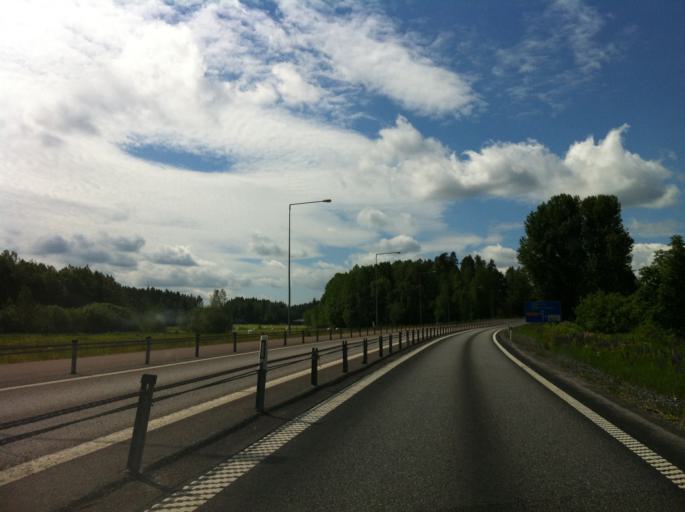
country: SE
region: Vaermland
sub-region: Grums Kommun
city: Slottsbron
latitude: 59.3199
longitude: 13.1057
